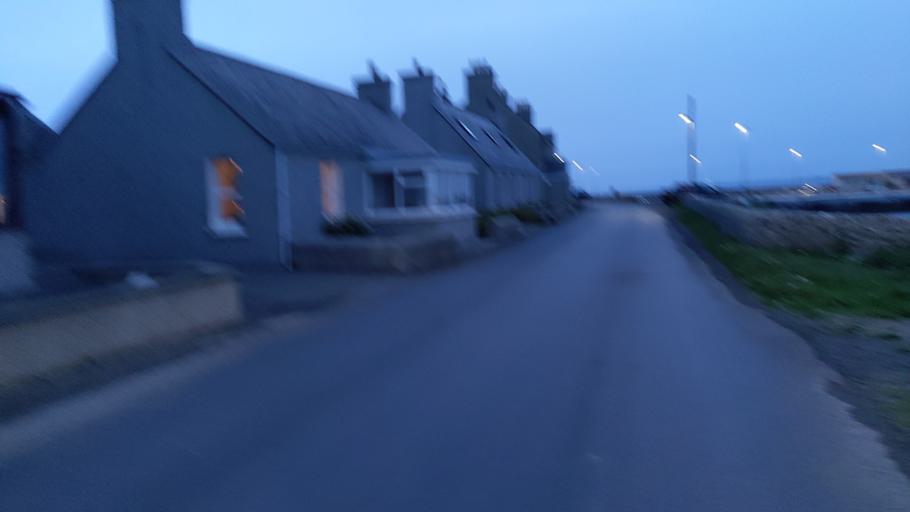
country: GB
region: Scotland
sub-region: Orkney Islands
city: Kirkwall
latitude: 59.3248
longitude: -2.9768
